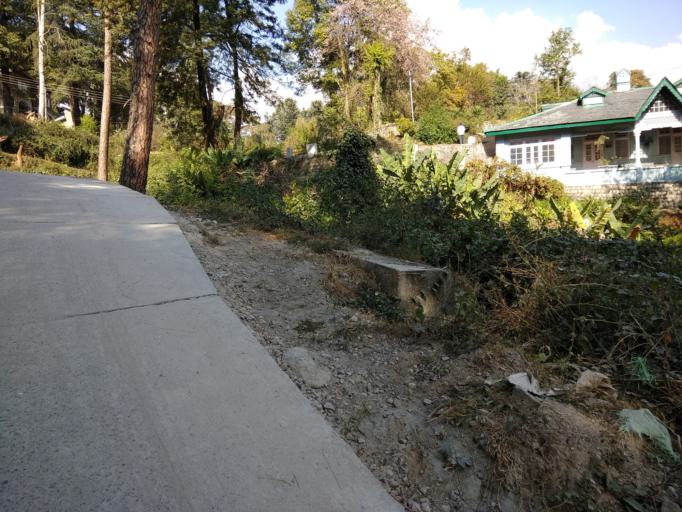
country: IN
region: Himachal Pradesh
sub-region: Kangra
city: Palampur
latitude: 32.1121
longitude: 76.5380
